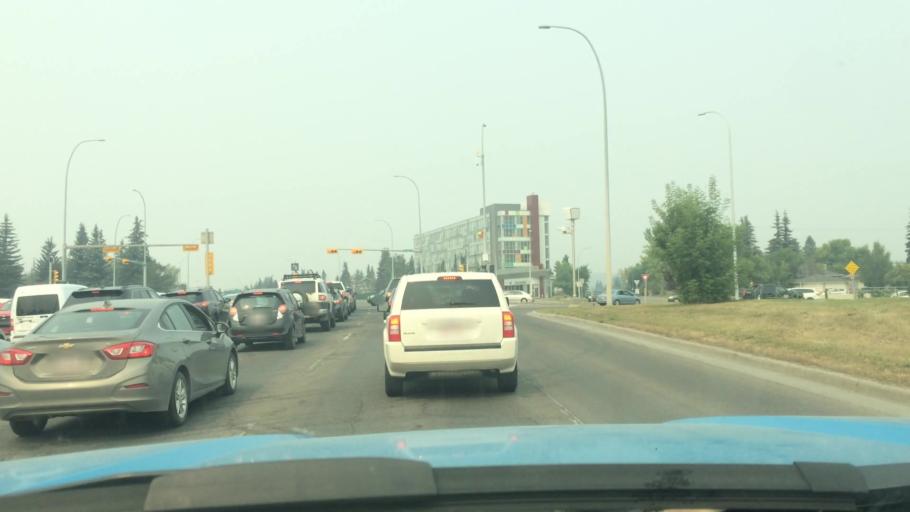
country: CA
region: Alberta
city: Calgary
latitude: 51.0735
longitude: -114.1179
